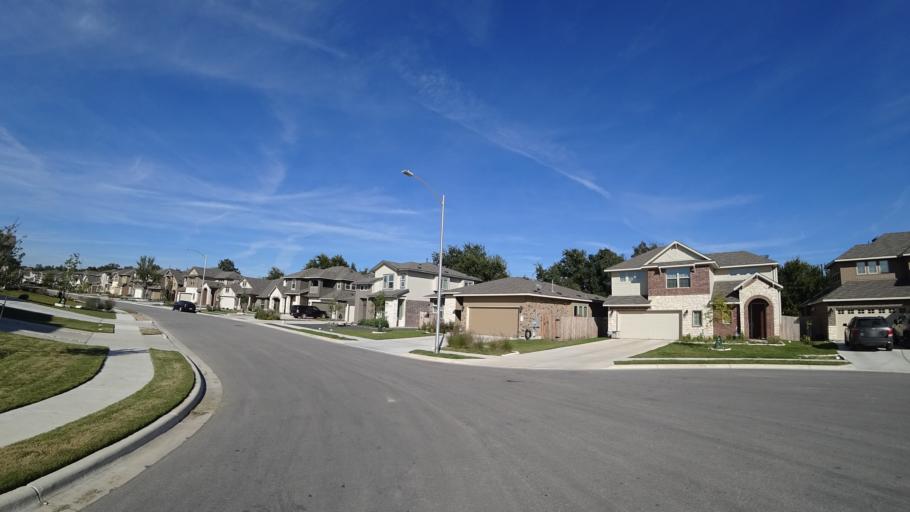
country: US
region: Texas
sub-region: Travis County
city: Austin
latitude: 30.2564
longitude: -97.6706
